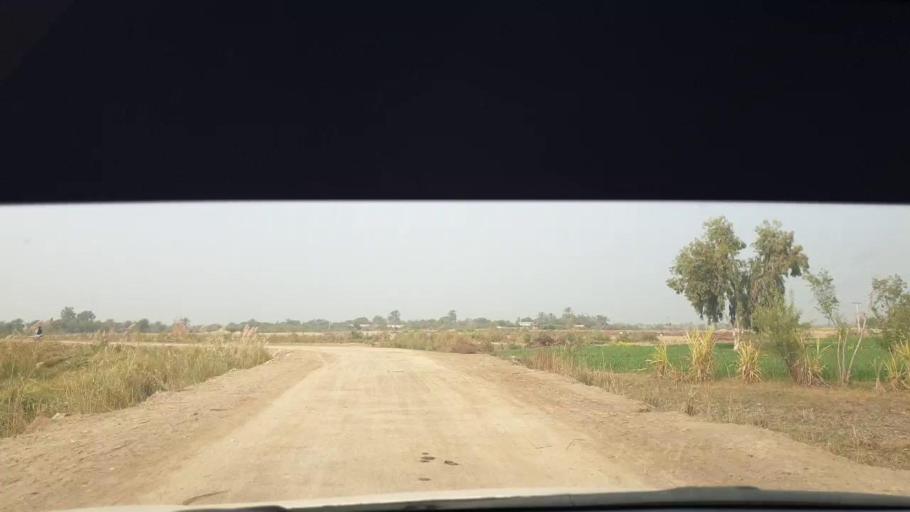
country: PK
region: Sindh
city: Berani
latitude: 25.8202
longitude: 68.8424
